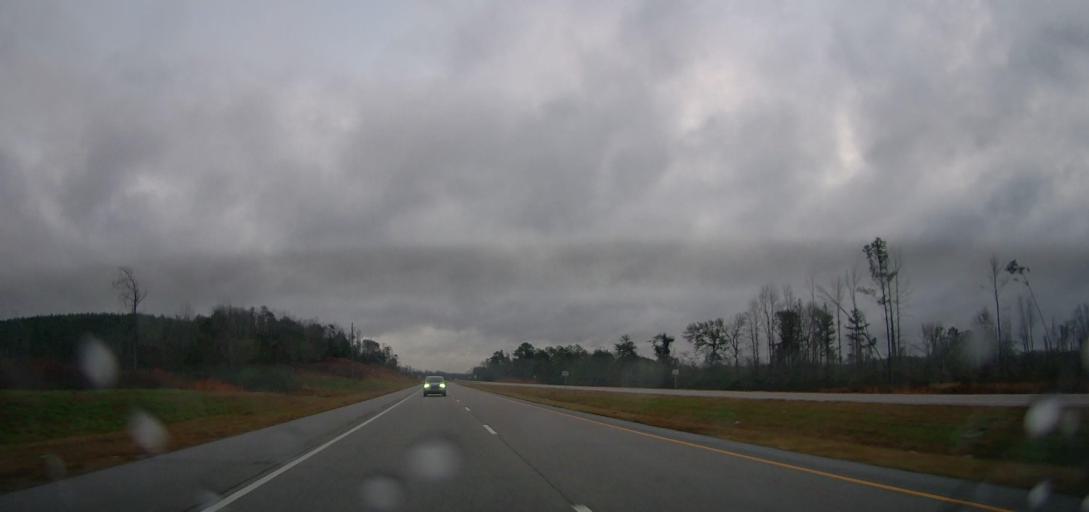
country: US
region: Alabama
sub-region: Bibb County
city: Centreville
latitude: 32.9454
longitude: -87.0896
